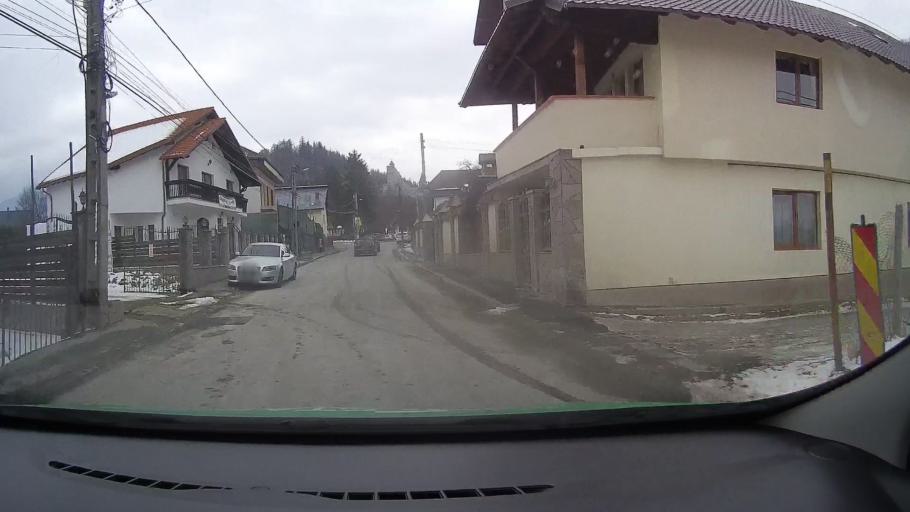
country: RO
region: Brasov
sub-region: Comuna Bran
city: Bran
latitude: 45.5184
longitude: 25.3665
